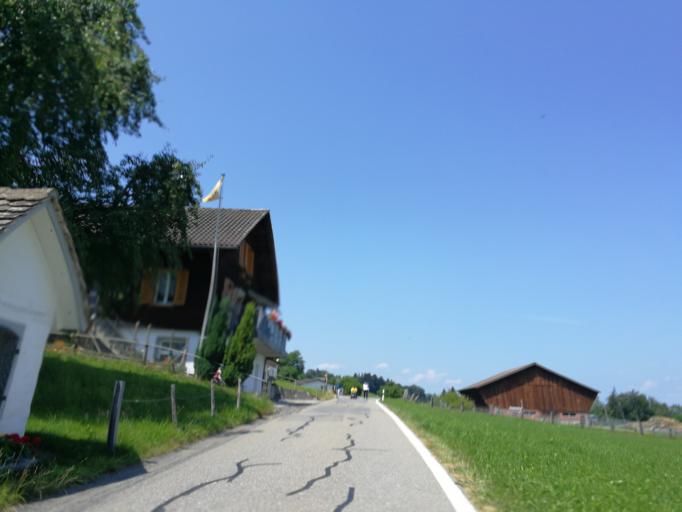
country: CH
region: Schwyz
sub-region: Bezirk March
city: Altendorf
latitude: 47.1839
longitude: 8.7939
